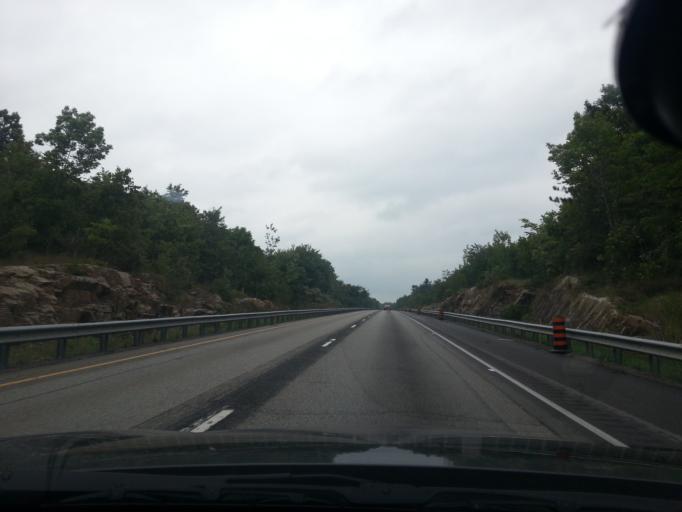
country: US
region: New York
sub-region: Jefferson County
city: Alexandria Bay
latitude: 44.4061
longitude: -75.9300
